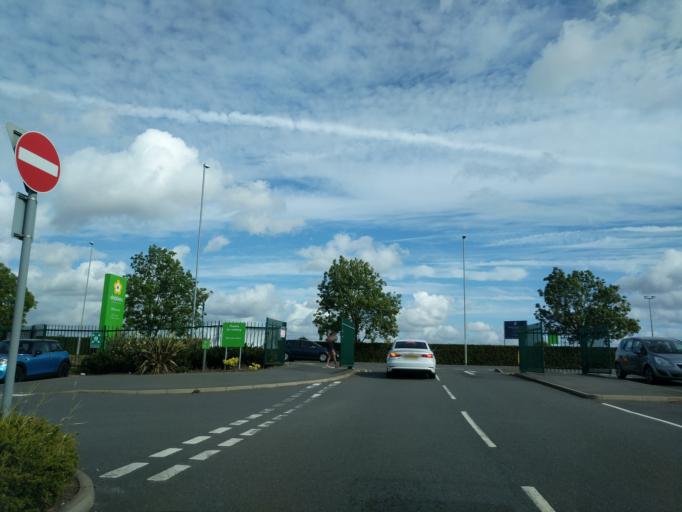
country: GB
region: England
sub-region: Northamptonshire
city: Hardingstone
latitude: 52.2104
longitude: -0.8916
